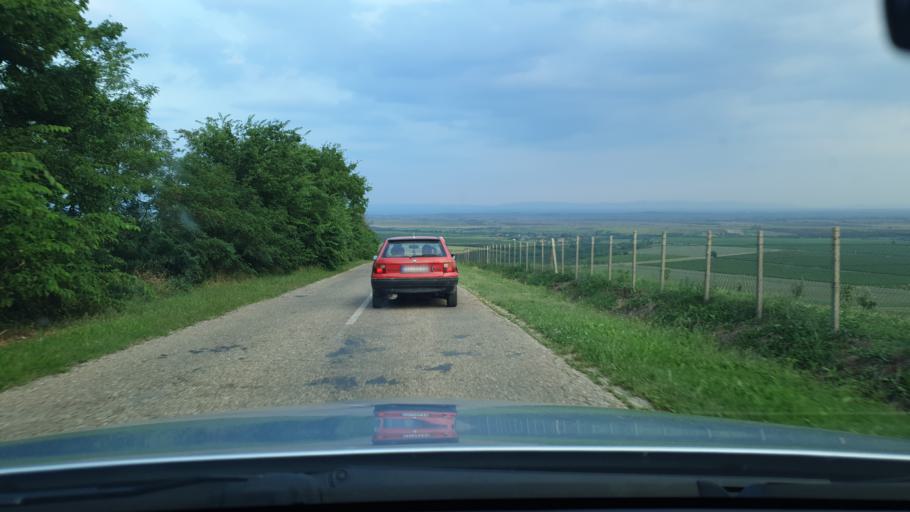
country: RS
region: Autonomna Pokrajina Vojvodina
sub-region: Juznobanatski Okrug
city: Vrsac
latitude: 45.1142
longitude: 21.3245
